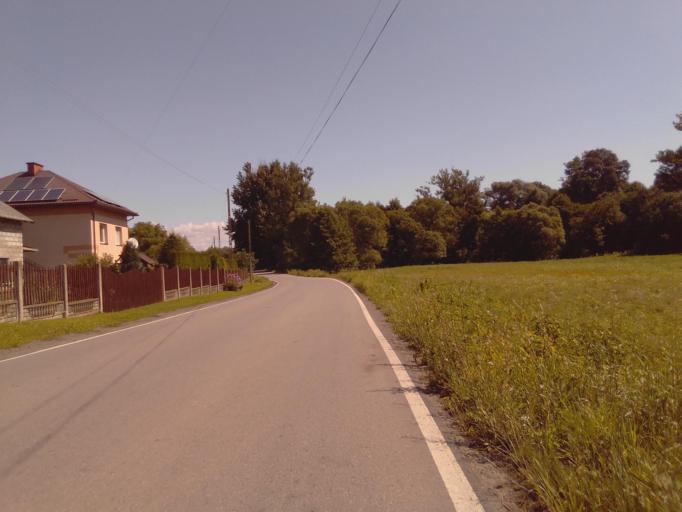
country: PL
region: Subcarpathian Voivodeship
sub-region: Powiat krosnienski
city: Jedlicze
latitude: 49.6944
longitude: 21.6143
